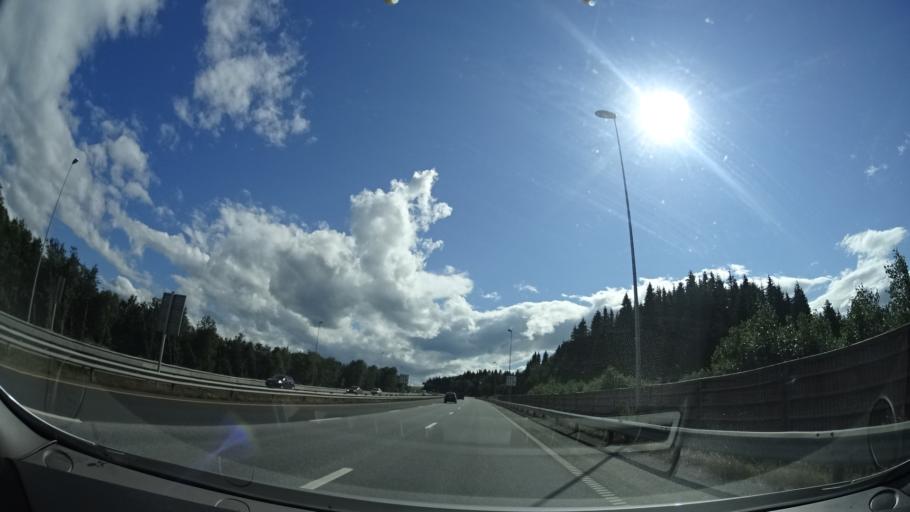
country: NO
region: Sor-Trondelag
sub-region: Trondheim
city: Trondheim
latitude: 63.3847
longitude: 10.3767
